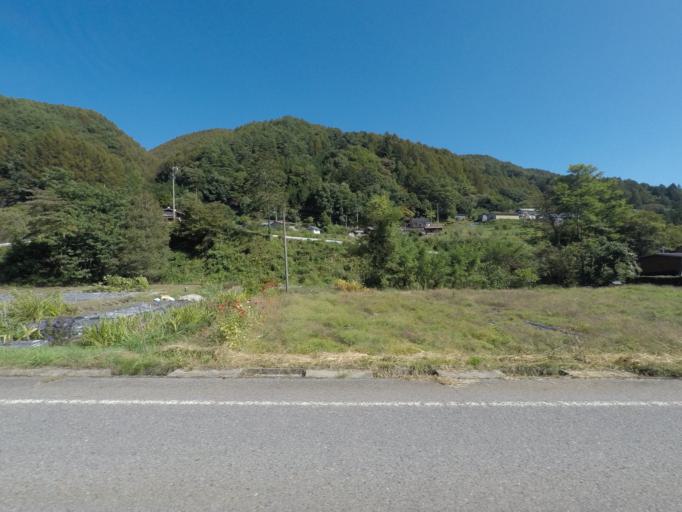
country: JP
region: Nagano
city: Tatsuno
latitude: 35.9744
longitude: 137.7518
